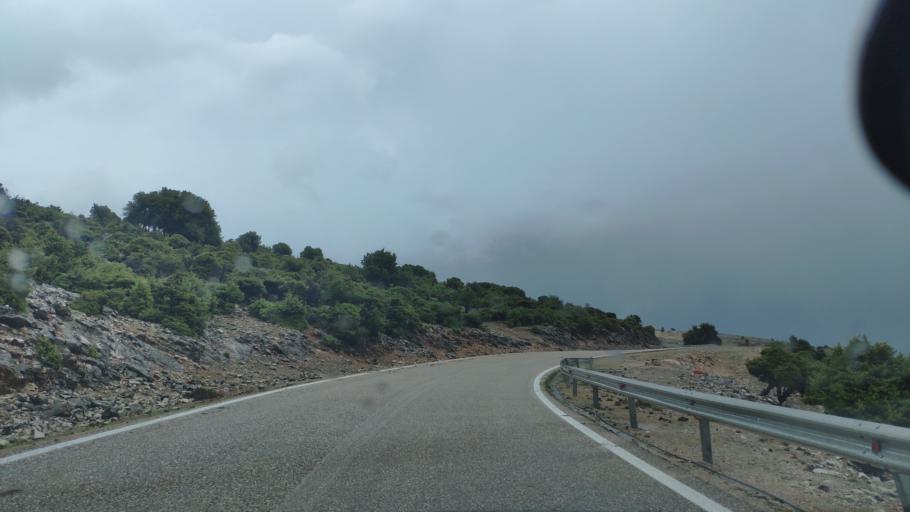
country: GR
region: West Greece
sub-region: Nomos Aitolias kai Akarnanias
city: Krikellos
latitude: 39.0719
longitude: 21.3848
